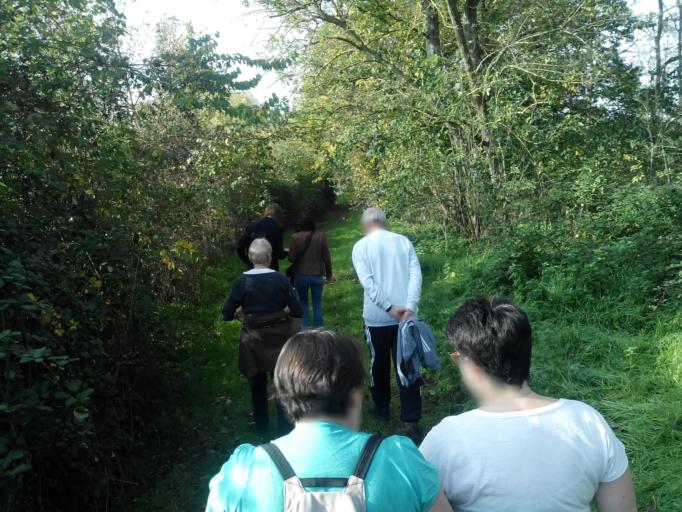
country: FR
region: Centre
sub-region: Departement d'Indre-et-Loire
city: Fondettes
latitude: 47.3846
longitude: 0.6174
